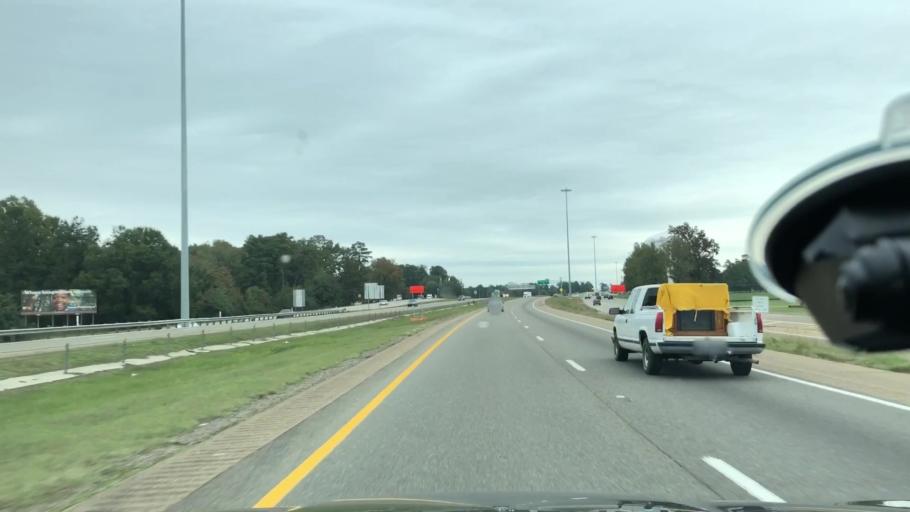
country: US
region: Arkansas
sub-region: Miller County
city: Texarkana
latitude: 33.4683
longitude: -94.0597
